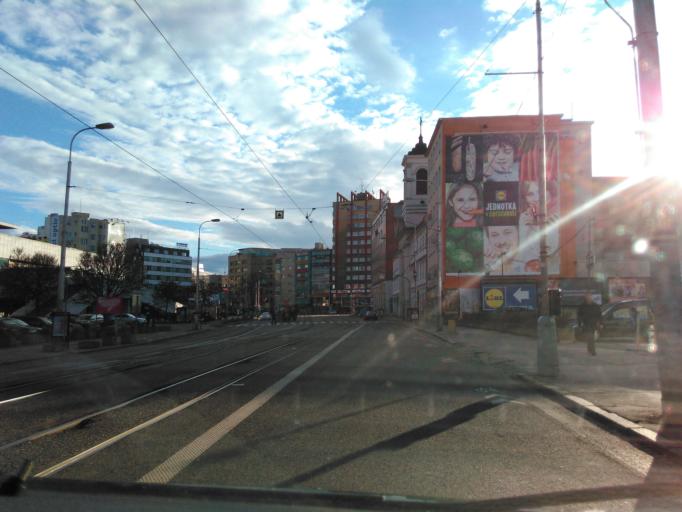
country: SK
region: Bratislavsky
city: Bratislava
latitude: 48.1462
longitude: 17.1141
